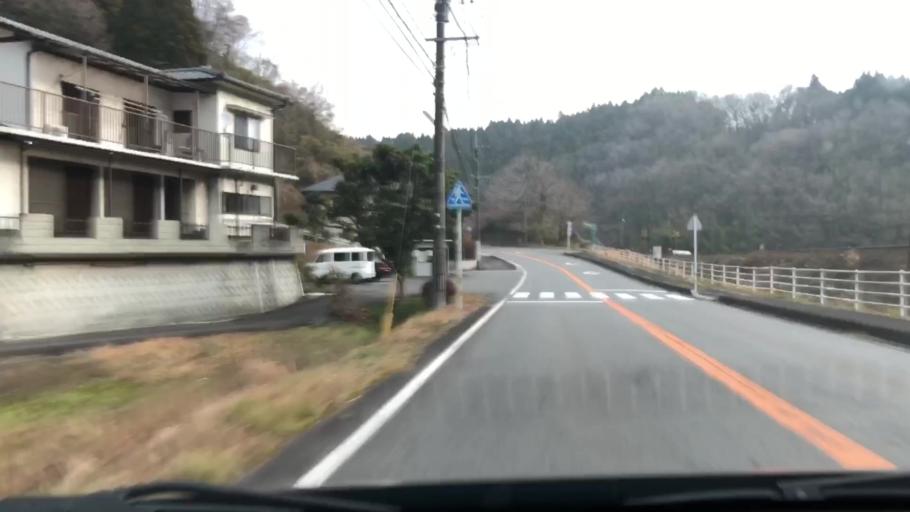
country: JP
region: Oita
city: Takedamachi
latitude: 32.9741
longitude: 131.5276
